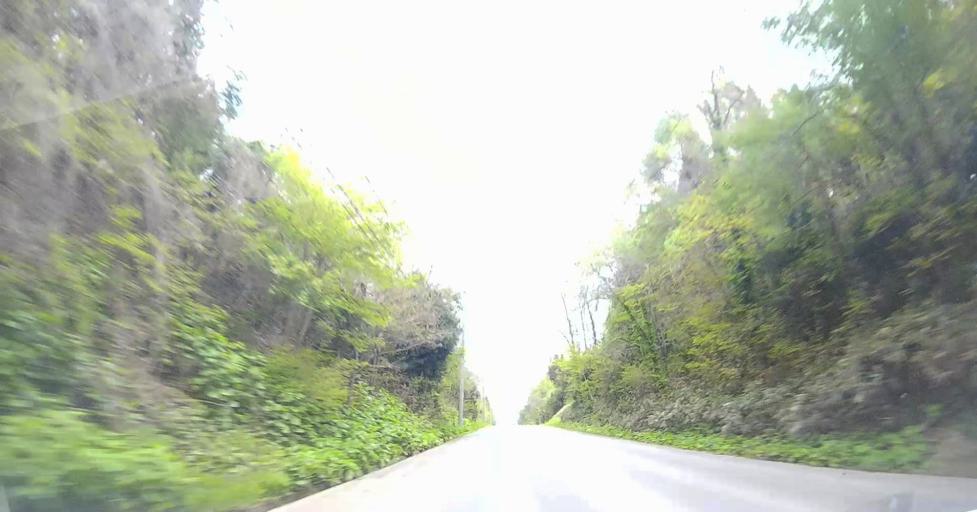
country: JP
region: Aomori
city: Shimokizukuri
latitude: 41.1785
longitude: 140.4719
